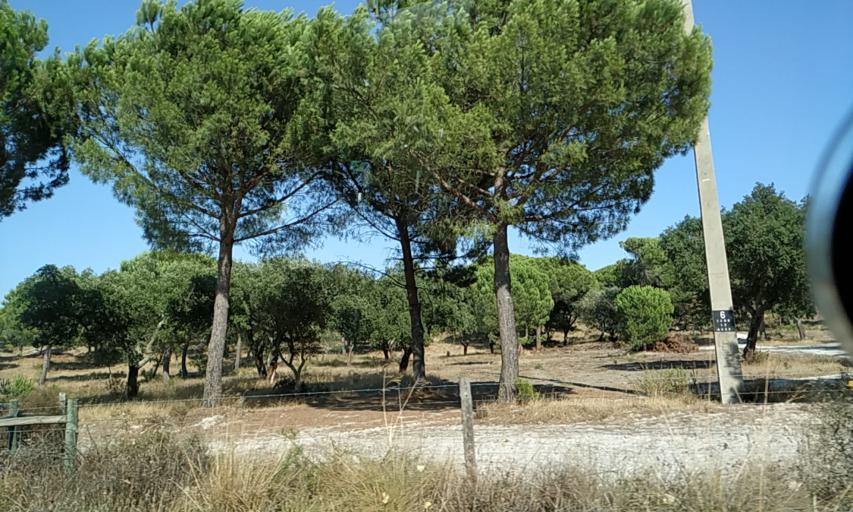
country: PT
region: Santarem
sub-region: Coruche
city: Coruche
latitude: 38.8802
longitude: -8.5398
